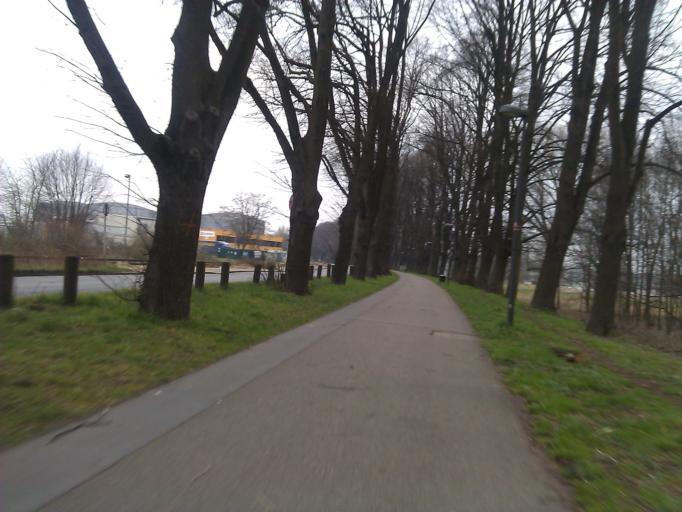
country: DE
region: North Rhine-Westphalia
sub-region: Regierungsbezirk Koln
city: Muelheim
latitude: 50.9754
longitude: 6.9905
